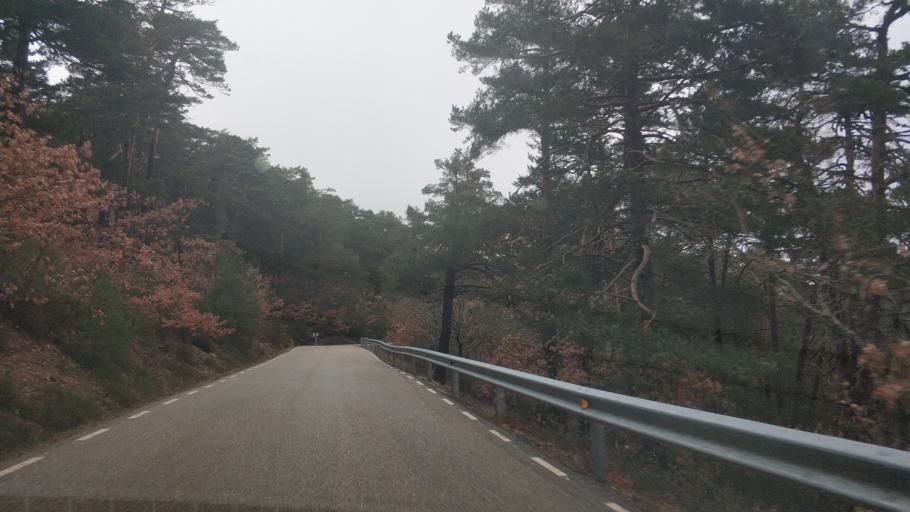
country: ES
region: Castille and Leon
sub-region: Provincia de Burgos
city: Quintanar de la Sierra
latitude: 42.0051
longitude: -3.0199
